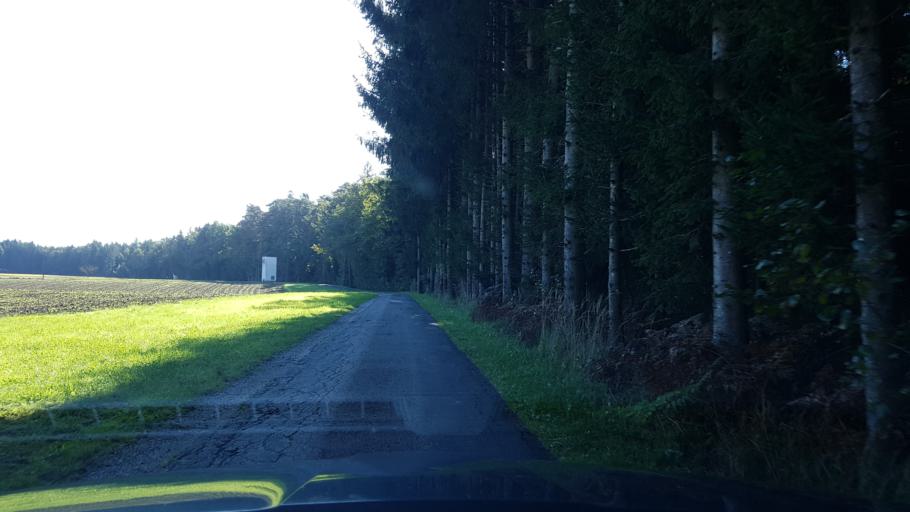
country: AT
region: Styria
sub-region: Politischer Bezirk Deutschlandsberg
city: Sankt Martin im Sulmtal
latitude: 46.7431
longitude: 15.2963
